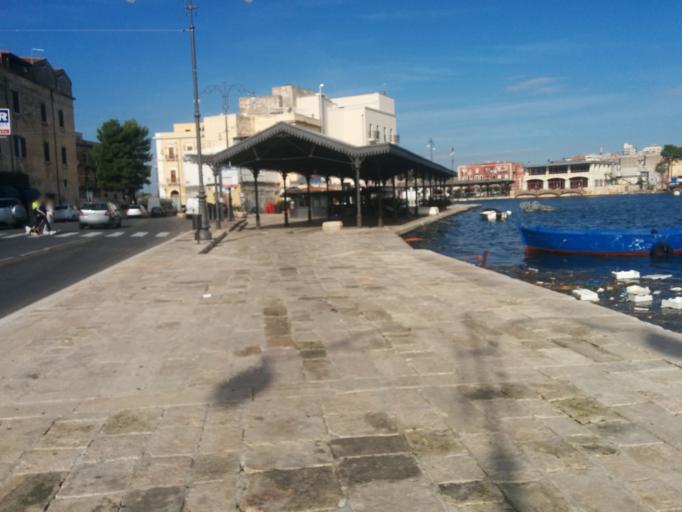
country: IT
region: Apulia
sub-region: Provincia di Taranto
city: Statte
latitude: 40.4787
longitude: 17.2285
